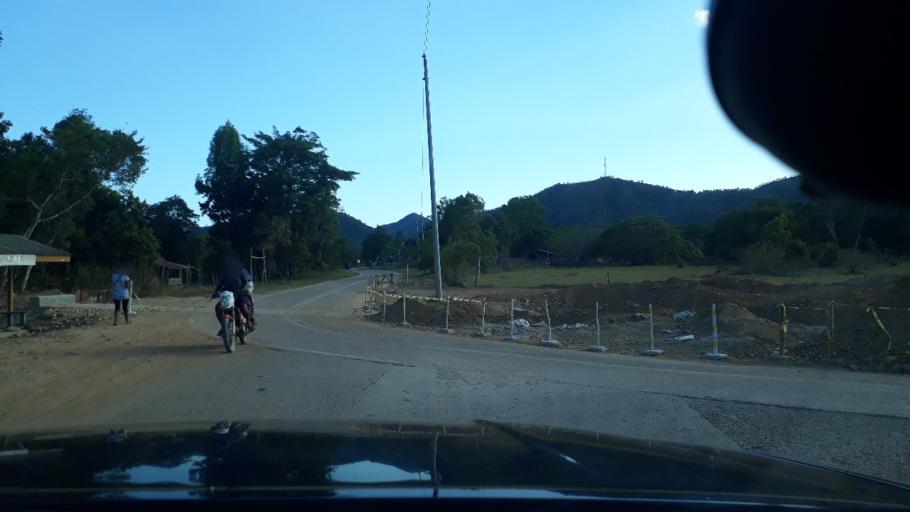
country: PH
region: Mimaropa
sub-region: Province of Palawan
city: Coron
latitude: 12.1169
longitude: 120.1019
